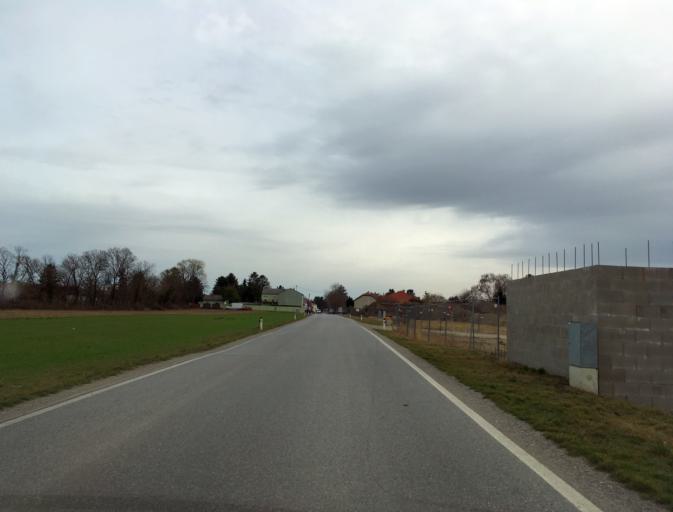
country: AT
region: Lower Austria
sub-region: Politischer Bezirk Ganserndorf
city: Leopoldsdorf im Marchfelde
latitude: 48.2272
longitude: 16.6831
